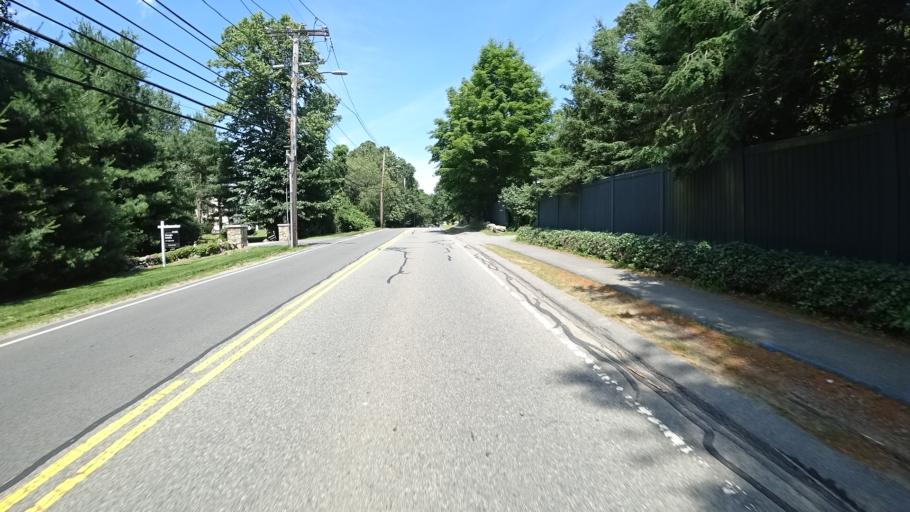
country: US
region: Massachusetts
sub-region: Norfolk County
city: Dedham
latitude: 42.2486
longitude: -71.1906
